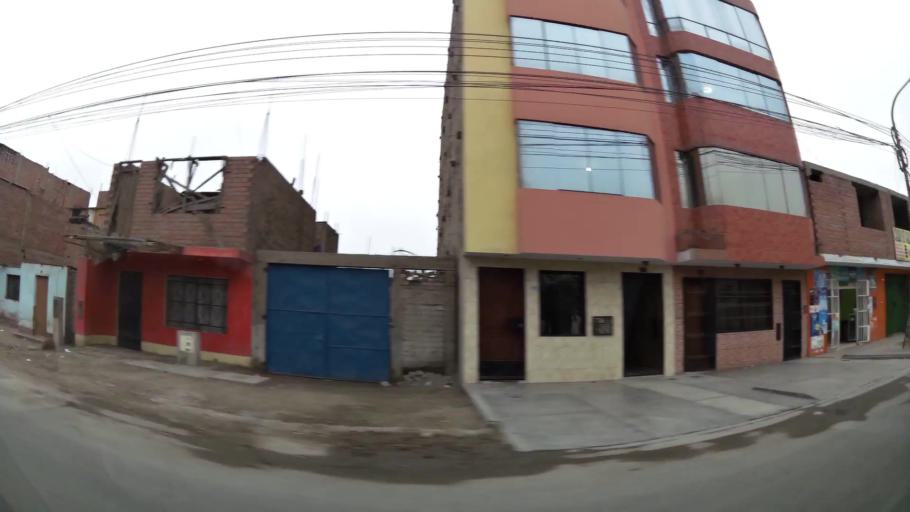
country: PE
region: Lima
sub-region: Lima
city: Urb. Santo Domingo
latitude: -11.9234
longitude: -77.0544
